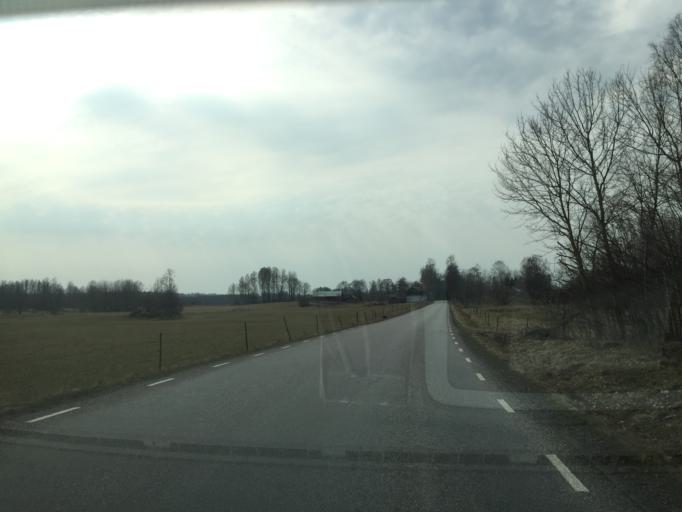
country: SE
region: Soedermanland
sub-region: Vingakers Kommun
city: Vingaker
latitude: 59.0446
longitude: 15.7624
